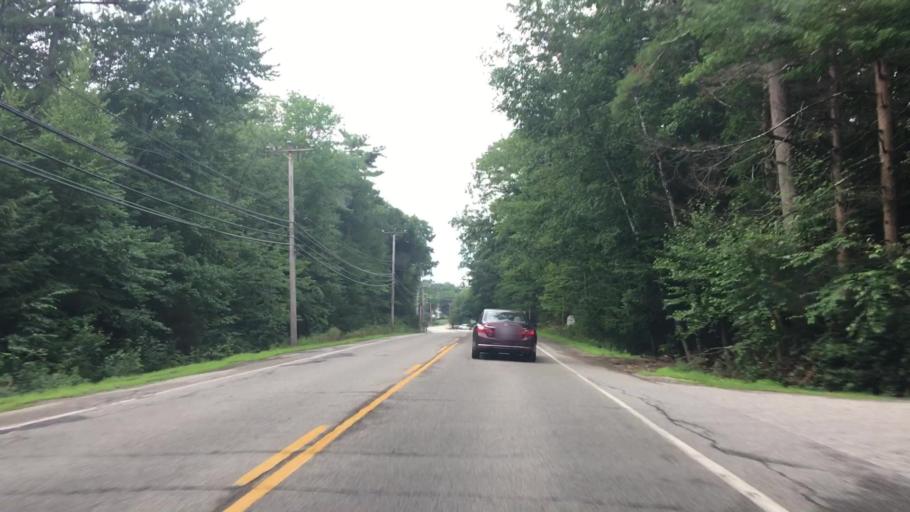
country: US
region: Maine
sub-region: York County
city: Sanford (historical)
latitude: 43.4544
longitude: -70.7655
